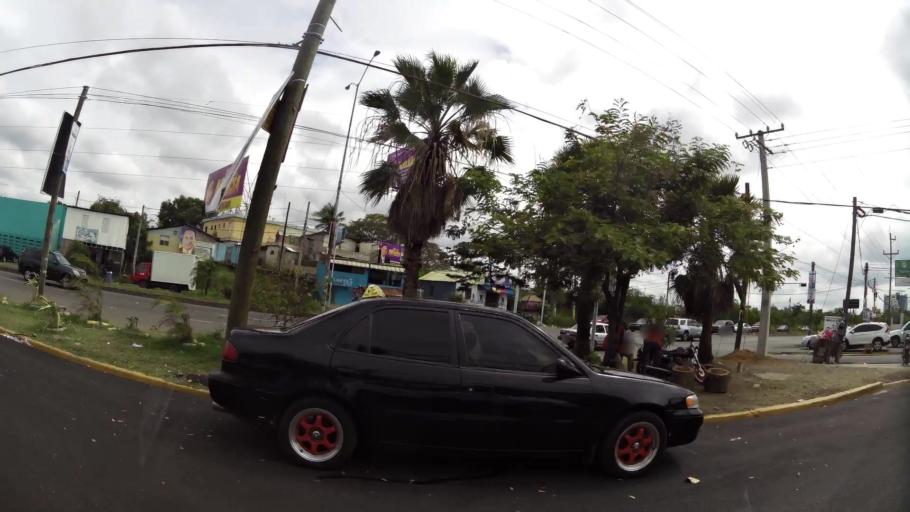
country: DO
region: Santiago
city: Santiago de los Caballeros
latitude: 19.4411
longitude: -70.6680
